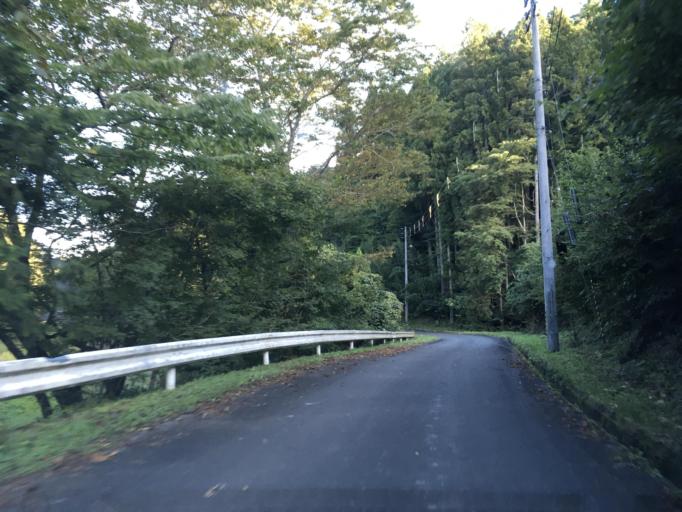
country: JP
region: Iwate
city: Ichinoseki
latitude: 38.7986
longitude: 141.4160
